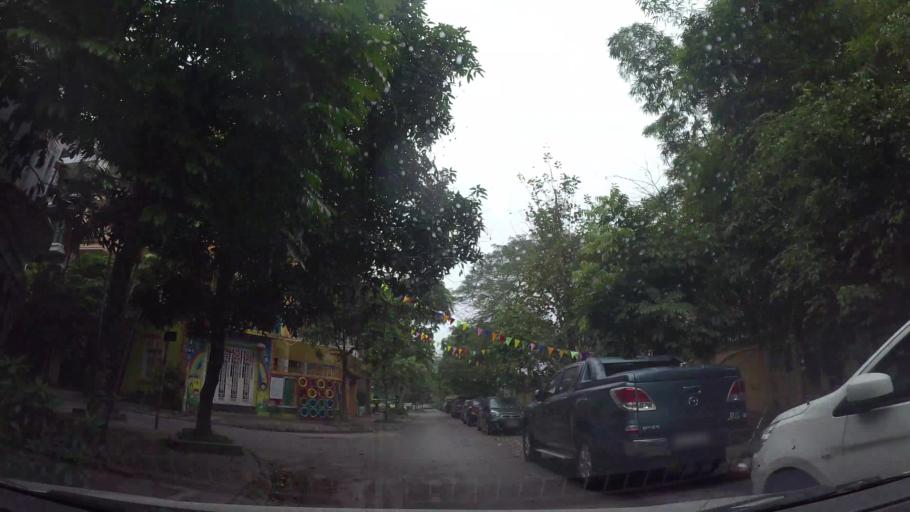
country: VN
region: Ha Noi
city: Cau Giay
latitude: 21.0140
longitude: 105.7983
